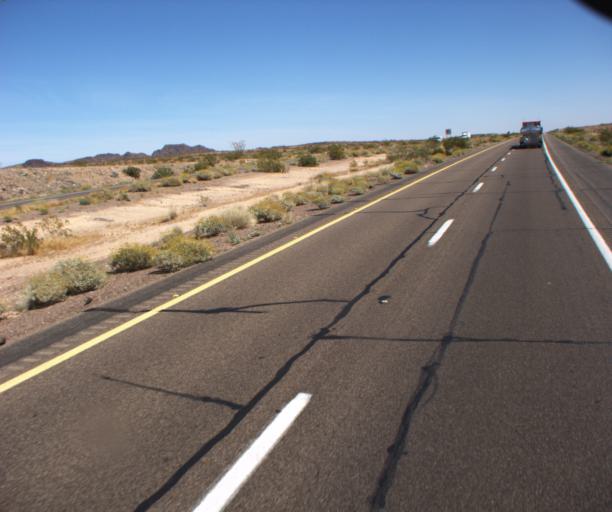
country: US
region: Arizona
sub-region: Maricopa County
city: Gila Bend
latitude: 32.8895
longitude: -113.0687
